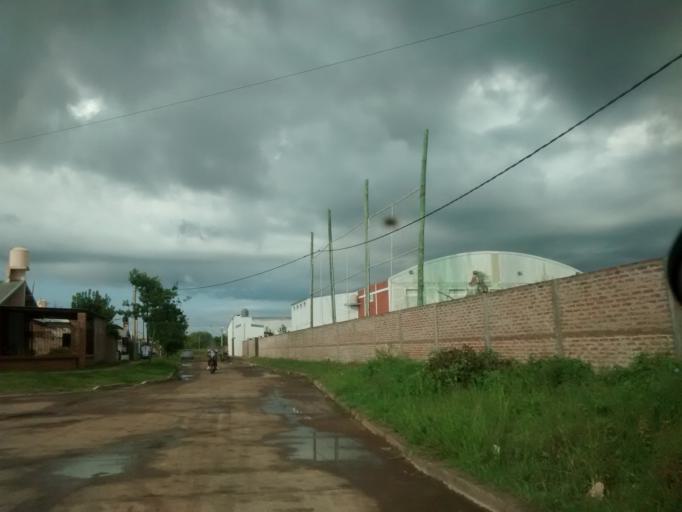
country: AR
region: Chaco
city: Puerto Tirol
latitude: -27.3792
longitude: -59.0924
